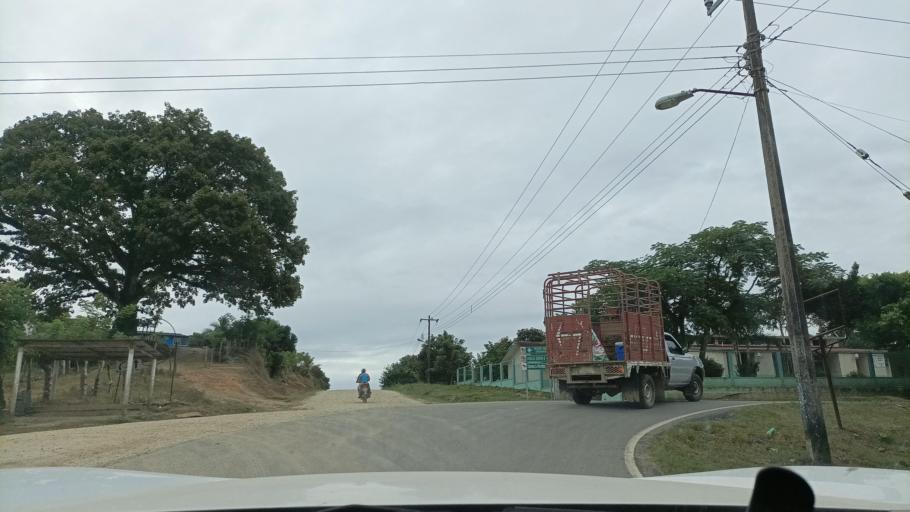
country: MX
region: Veracruz
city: Hidalgotitlan
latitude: 17.6580
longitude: -94.4040
